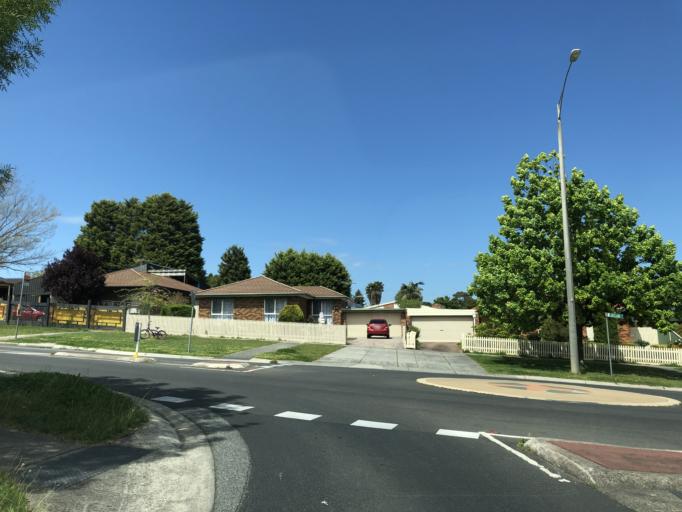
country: AU
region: Victoria
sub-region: Casey
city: Endeavour Hills
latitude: -37.9677
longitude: 145.2710
